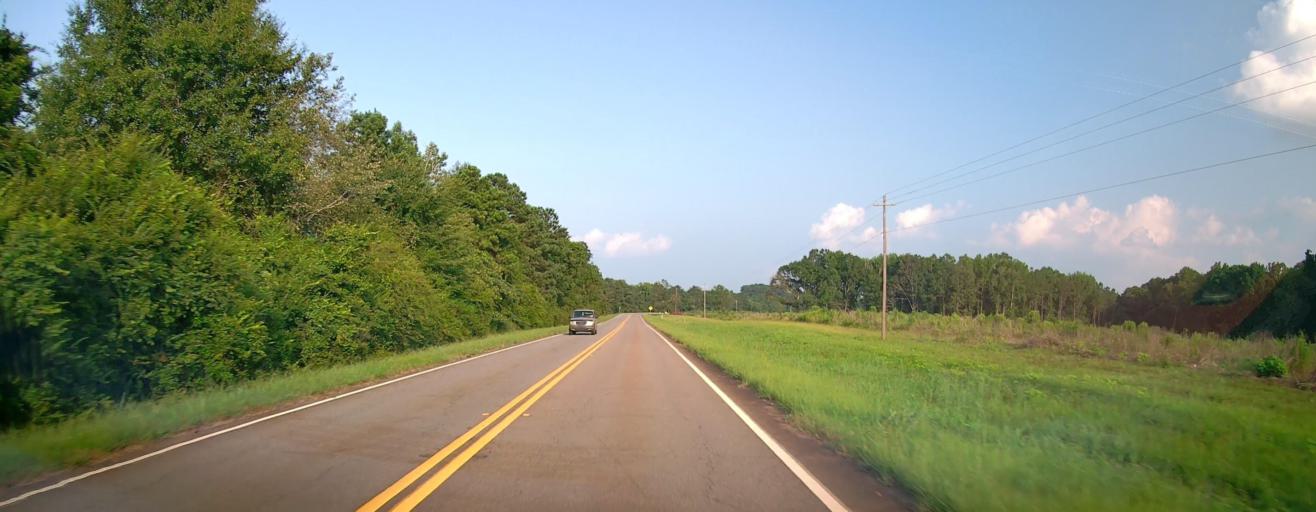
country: US
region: Georgia
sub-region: Jones County
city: Gray
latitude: 33.0602
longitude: -83.5664
